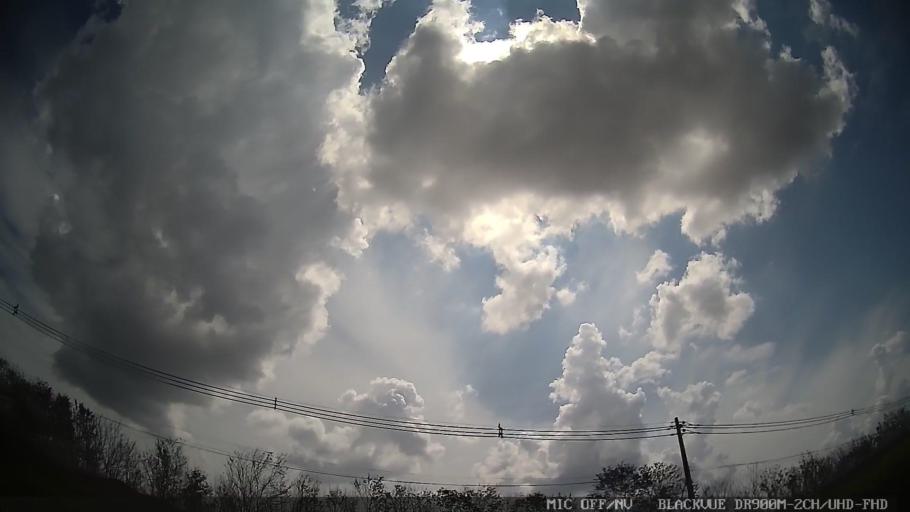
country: BR
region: Sao Paulo
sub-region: Braganca Paulista
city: Braganca Paulista
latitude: -22.9611
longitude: -46.5867
